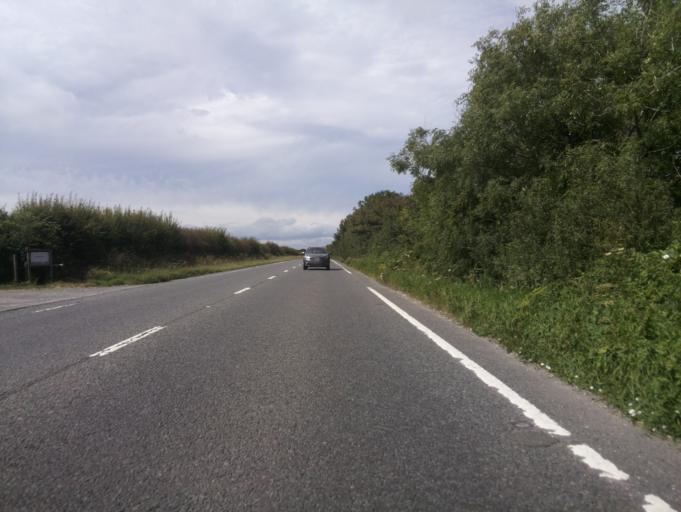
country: GB
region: England
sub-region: Dorset
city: Sherborne
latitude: 50.8072
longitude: -2.5526
